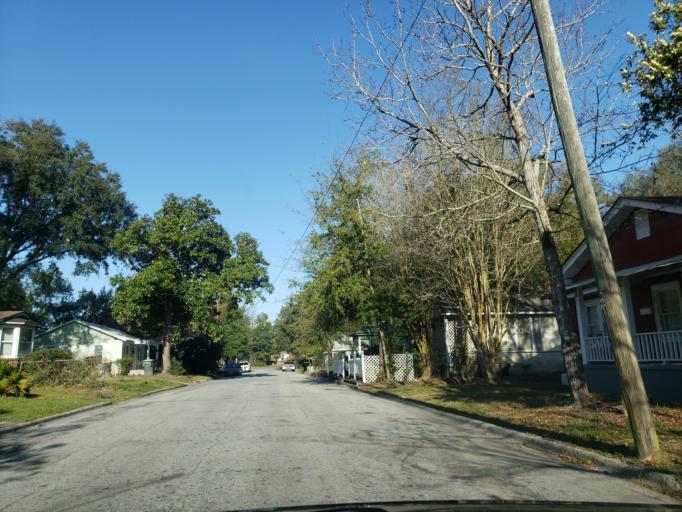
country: US
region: Georgia
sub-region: Chatham County
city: Thunderbolt
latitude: 32.0260
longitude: -81.0927
